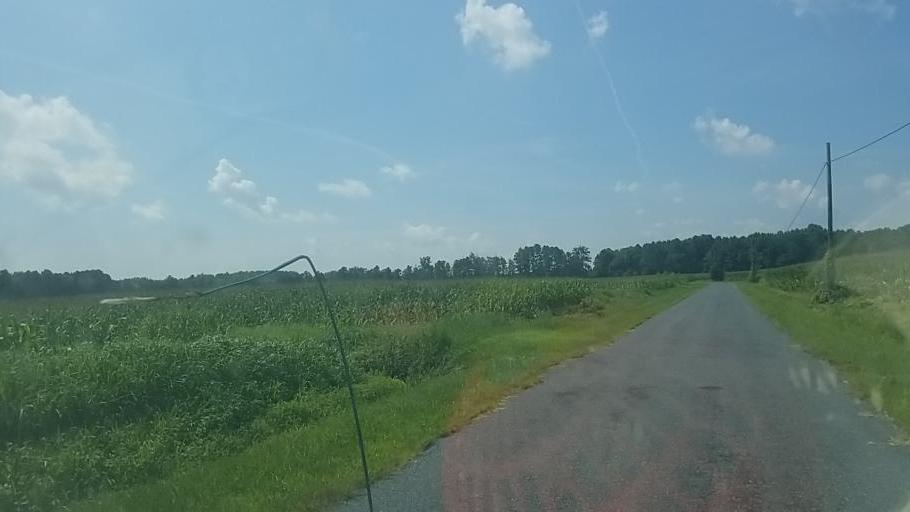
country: US
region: Maryland
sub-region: Worcester County
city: Berlin
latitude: 38.2935
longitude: -75.2946
